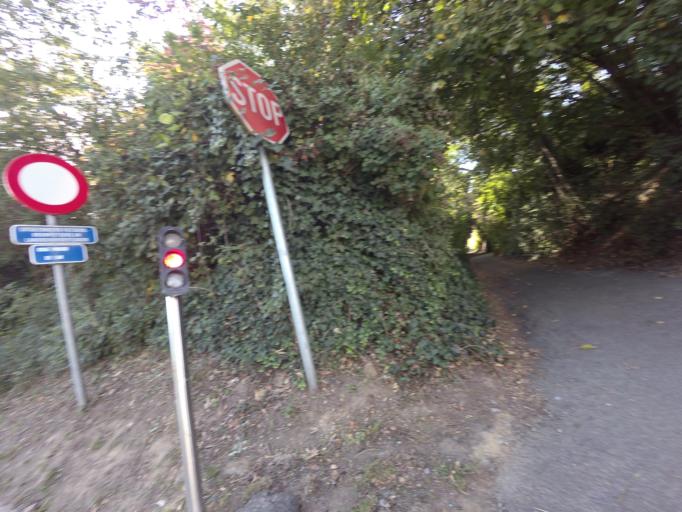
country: BE
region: Flanders
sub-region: Provincie Vlaams-Brabant
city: Kraainem
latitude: 50.8588
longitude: 4.4456
